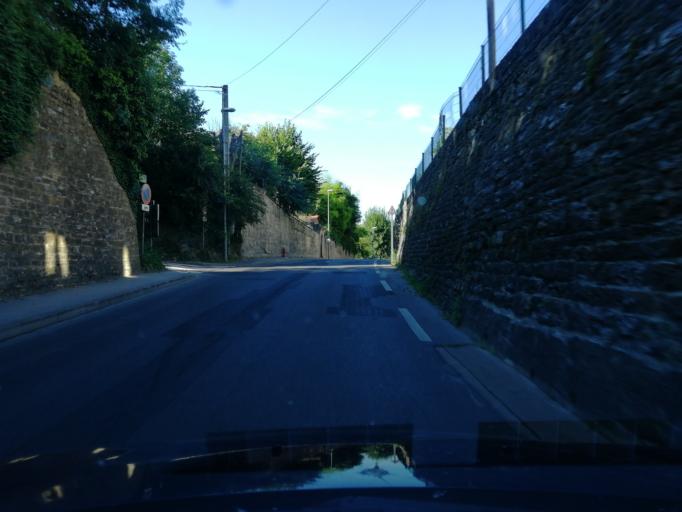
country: FR
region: Rhone-Alpes
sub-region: Departement du Rhone
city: Fontaines-sur-Saone
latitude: 45.8379
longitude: 4.8468
